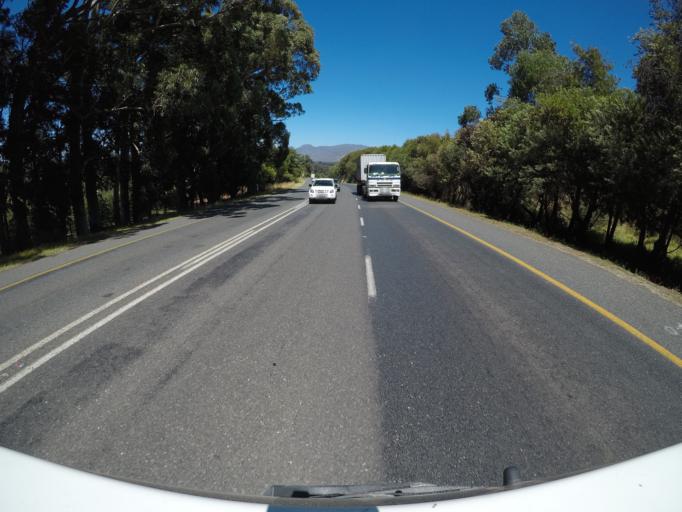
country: ZA
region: Western Cape
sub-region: Overberg District Municipality
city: Grabouw
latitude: -34.1631
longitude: 19.0286
